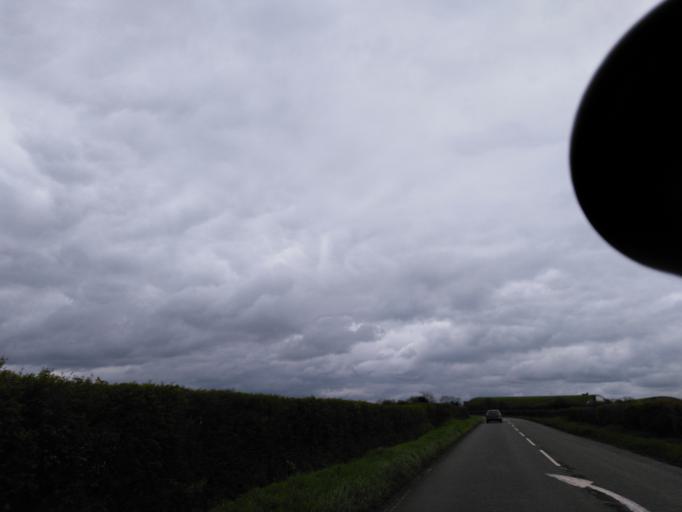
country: GB
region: England
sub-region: Wiltshire
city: Norton
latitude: 51.5400
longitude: -2.1287
